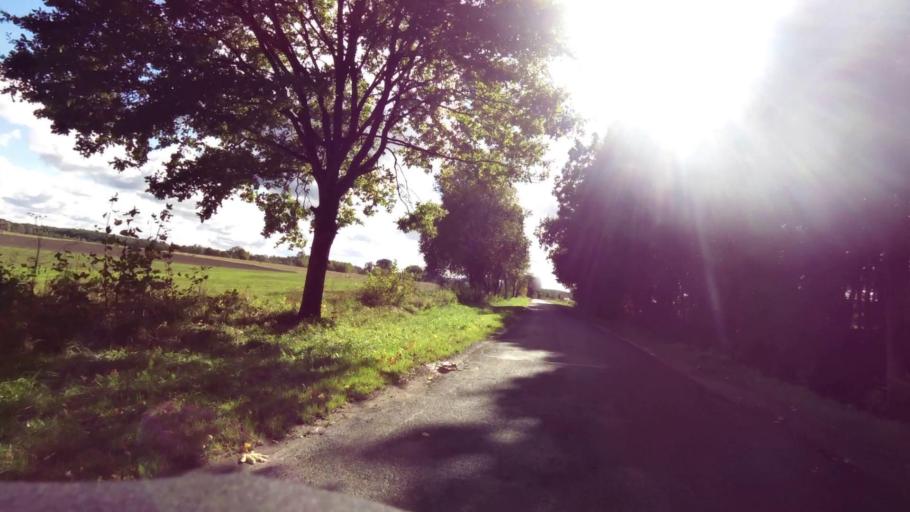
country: PL
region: West Pomeranian Voivodeship
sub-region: Powiat bialogardzki
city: Bialogard
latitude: 53.9960
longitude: 16.0628
